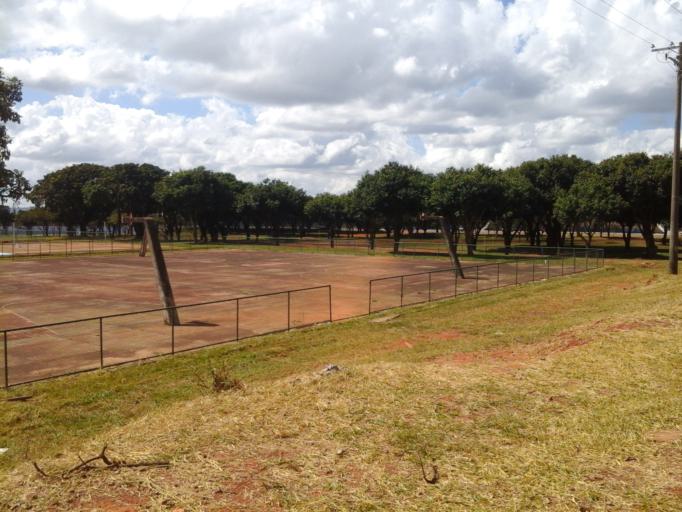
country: BR
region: Federal District
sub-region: Brasilia
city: Brasilia
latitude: -15.7814
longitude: -47.9031
